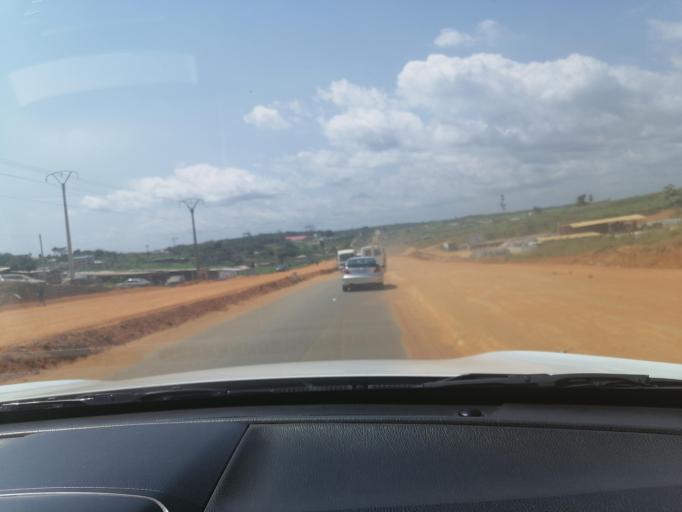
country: CI
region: Lagunes
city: Songon
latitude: 5.3433
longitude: -4.1533
